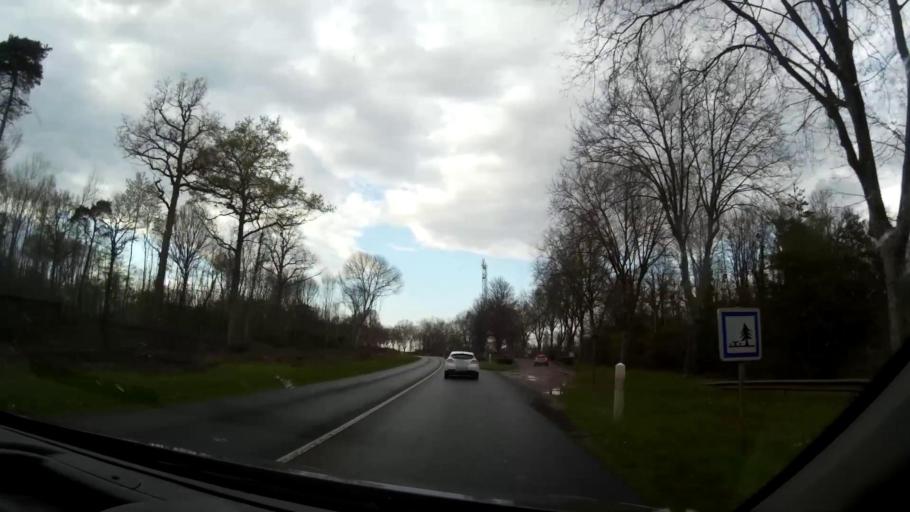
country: FR
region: Centre
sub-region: Departement du Loir-et-Cher
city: Cormeray
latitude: 47.4690
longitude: 1.4244
